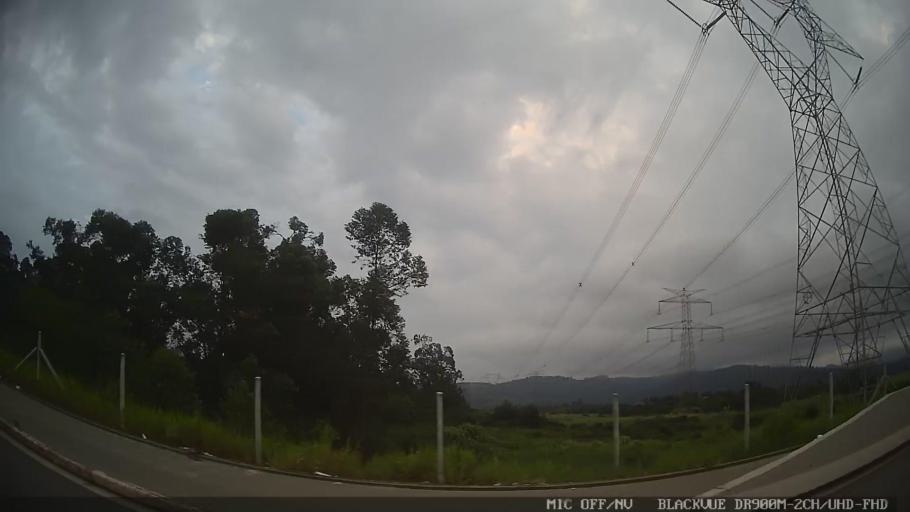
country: BR
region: Sao Paulo
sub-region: Mogi das Cruzes
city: Mogi das Cruzes
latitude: -23.5420
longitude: -46.2467
